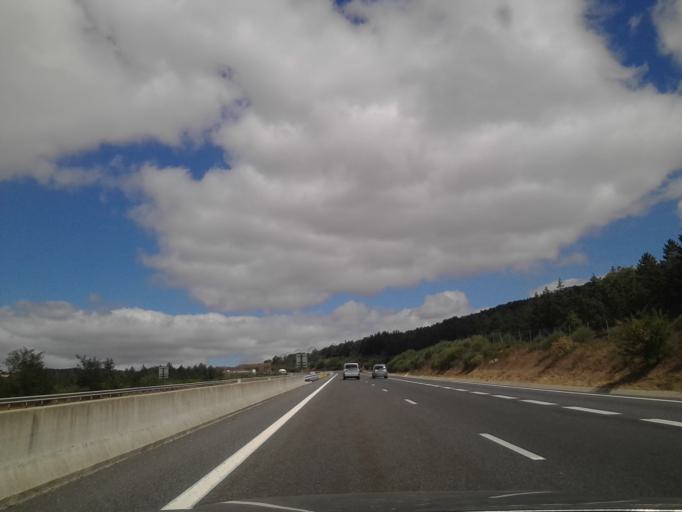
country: FR
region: Midi-Pyrenees
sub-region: Departement de l'Aveyron
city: Severac-le-Chateau
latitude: 44.2238
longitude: 3.0707
